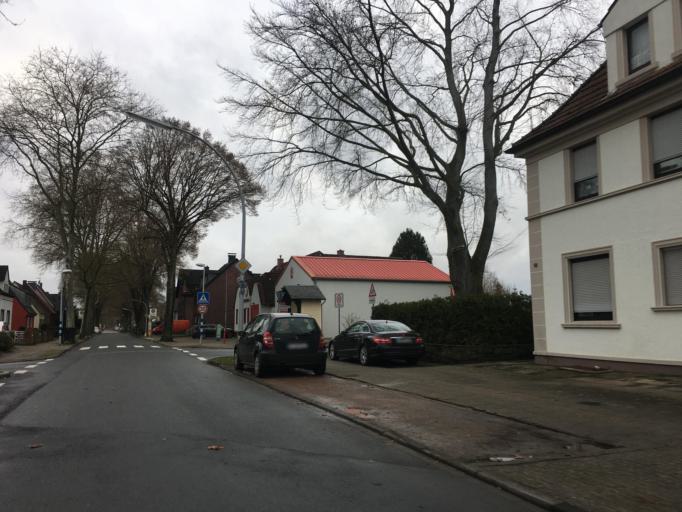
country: DE
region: North Rhine-Westphalia
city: Olfen
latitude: 51.7009
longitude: 7.3076
